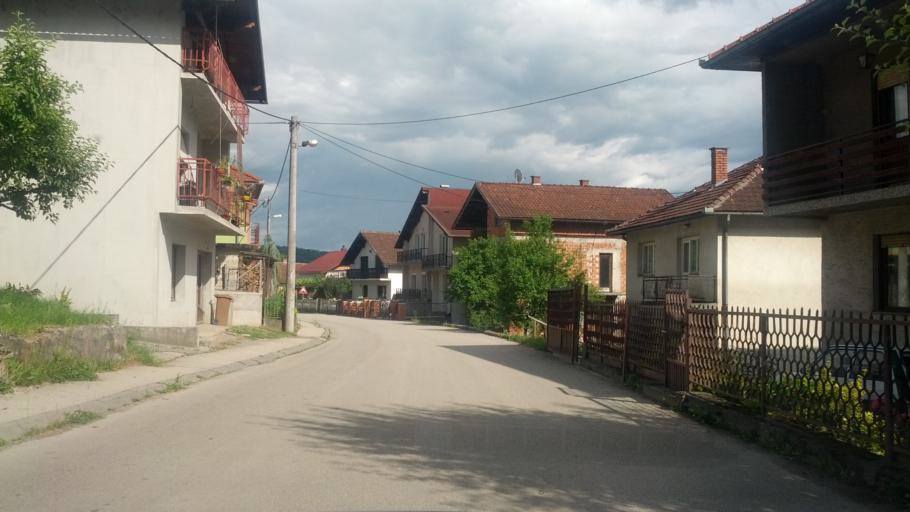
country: BA
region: Federation of Bosnia and Herzegovina
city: Bosanska Krupa
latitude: 44.8869
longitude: 16.1408
